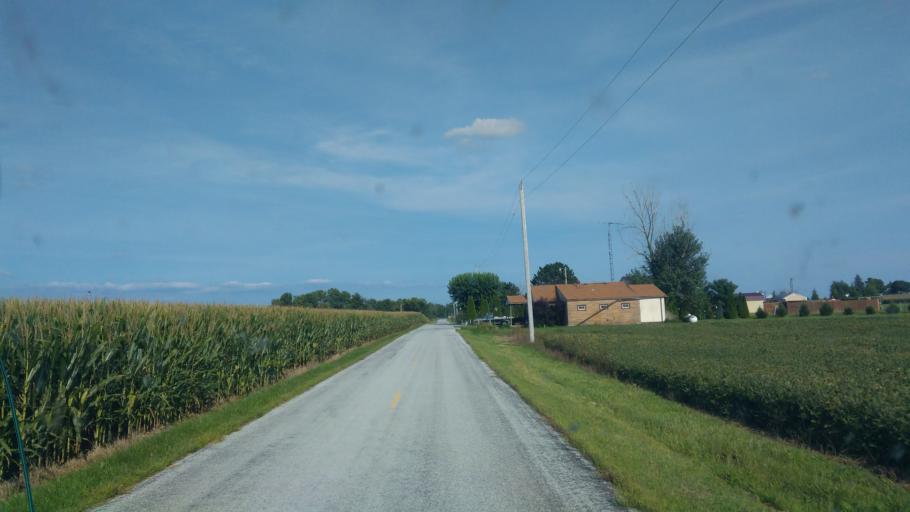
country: US
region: Ohio
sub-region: Hardin County
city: Kenton
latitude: 40.7099
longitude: -83.5768
